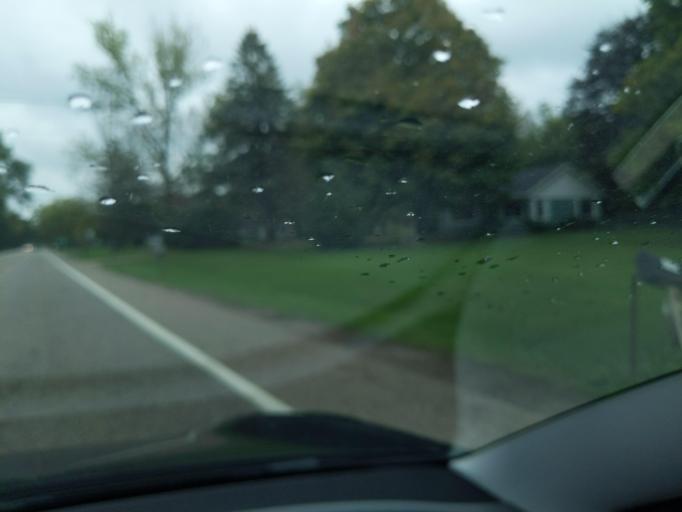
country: US
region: Michigan
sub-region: Eaton County
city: Charlotte
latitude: 42.5530
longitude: -84.8033
